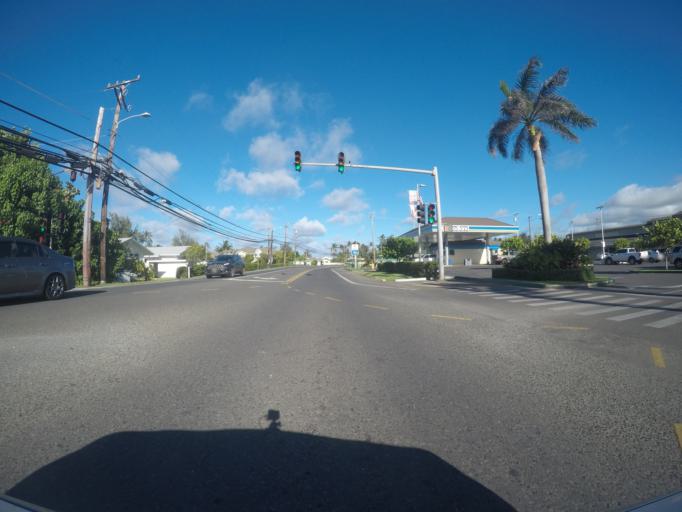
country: US
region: Hawaii
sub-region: Honolulu County
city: La'ie
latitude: 21.6470
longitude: -157.9213
